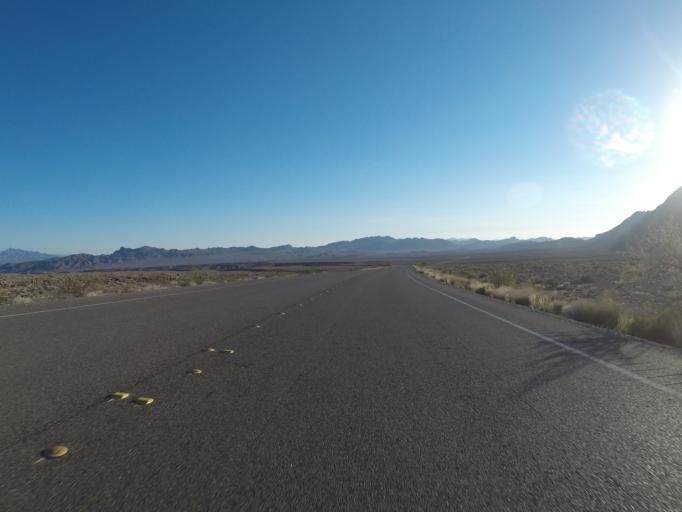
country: US
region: Nevada
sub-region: Clark County
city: Moapa Valley
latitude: 36.3541
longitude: -114.4827
